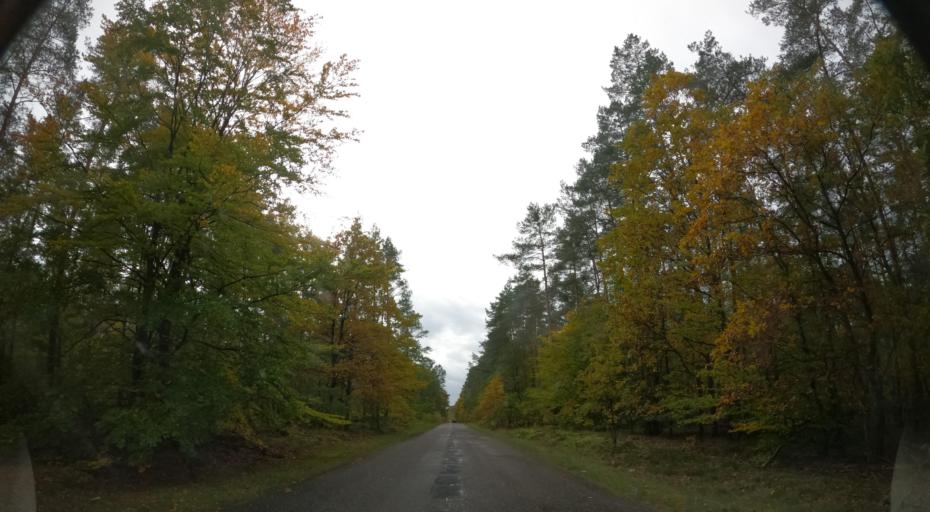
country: PL
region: West Pomeranian Voivodeship
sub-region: Powiat goleniowski
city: Stepnica
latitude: 53.6914
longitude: 14.6803
